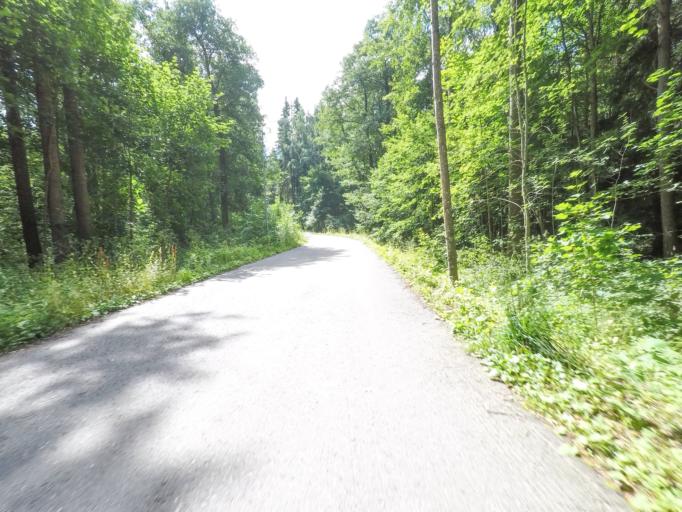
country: FI
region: Uusimaa
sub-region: Helsinki
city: Vantaa
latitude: 60.1648
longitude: 25.0901
